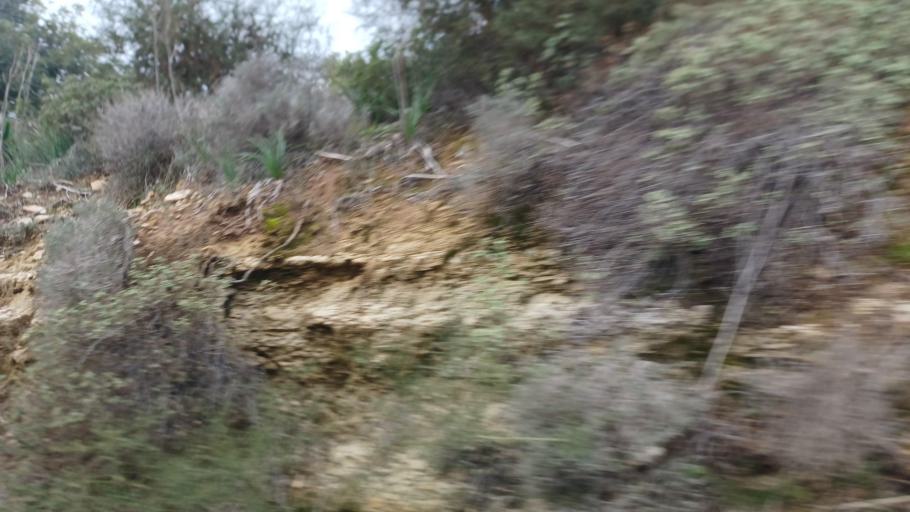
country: CY
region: Limassol
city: Pachna
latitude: 34.7467
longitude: 32.7338
